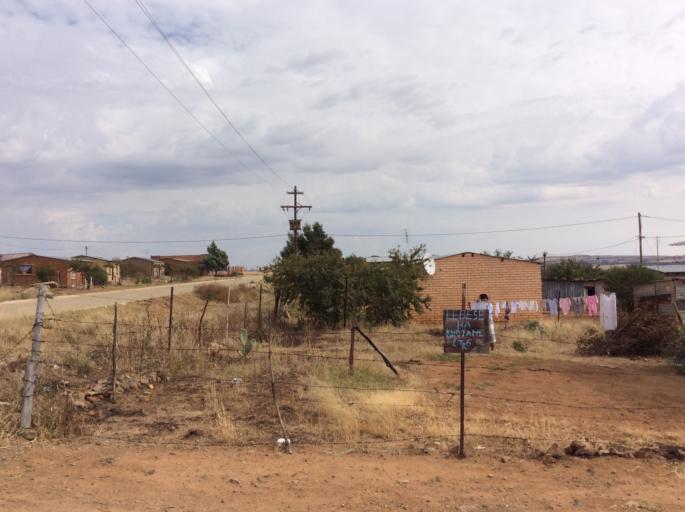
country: LS
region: Mafeteng
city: Mafeteng
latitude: -29.7215
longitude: 27.0082
